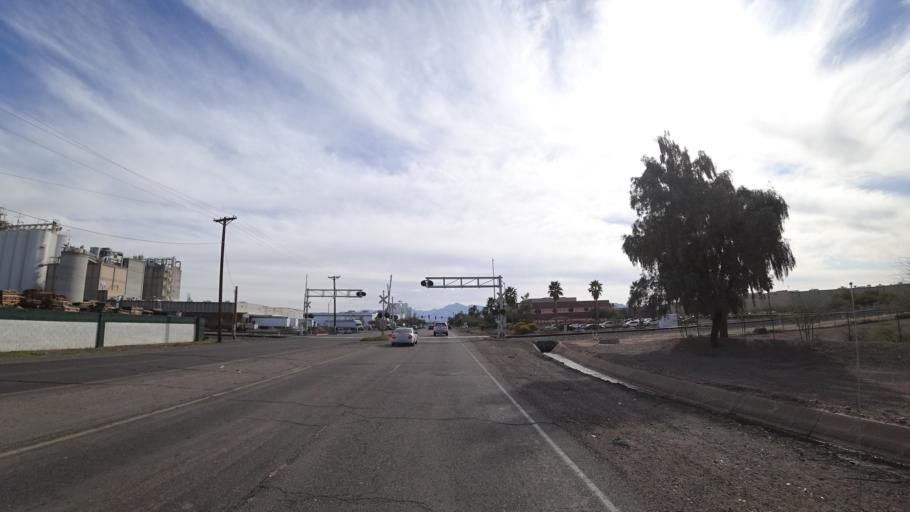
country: US
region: Arizona
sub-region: Maricopa County
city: Tolleson
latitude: 33.4435
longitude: -112.2725
